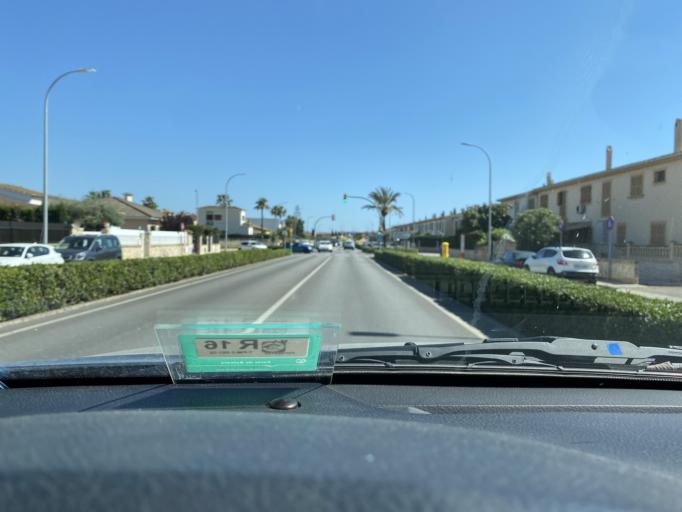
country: ES
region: Balearic Islands
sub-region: Illes Balears
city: Palma
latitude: 39.6107
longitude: 2.6848
